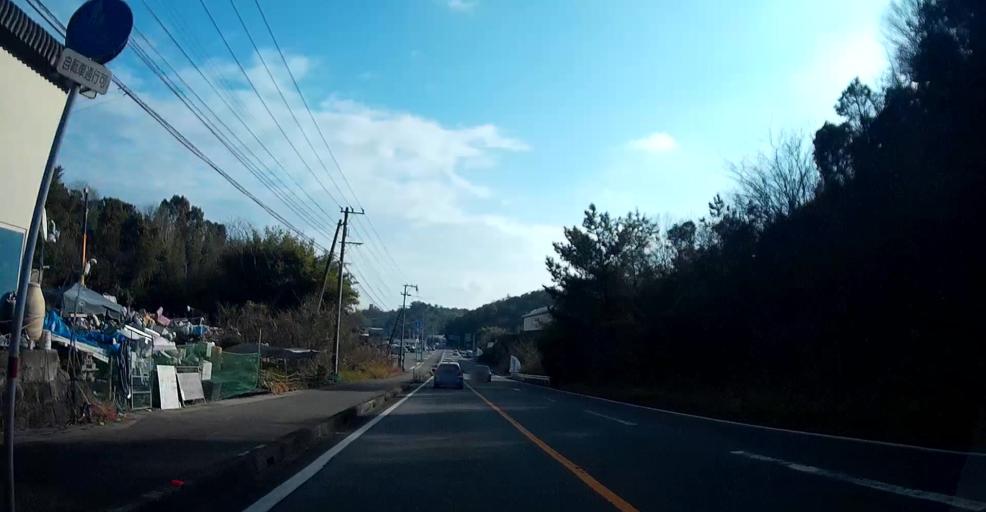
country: JP
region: Kumamoto
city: Yatsushiro
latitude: 32.5561
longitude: 130.4162
